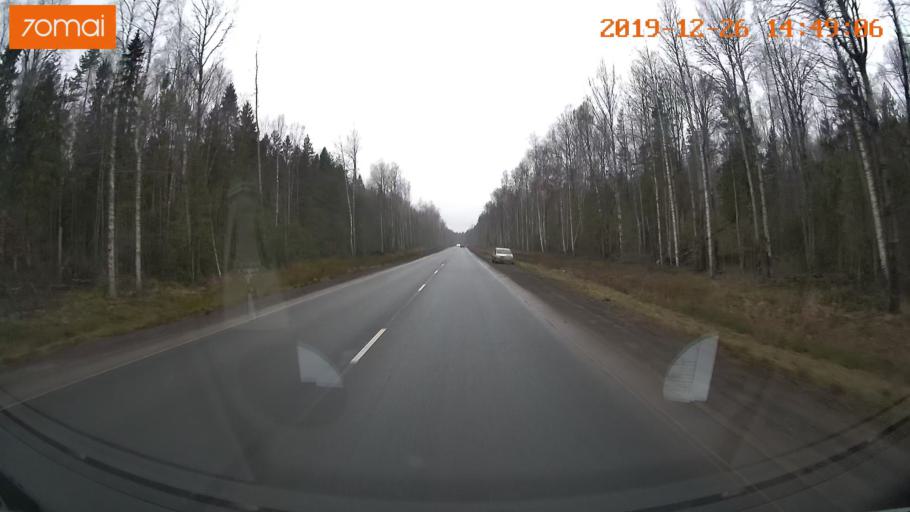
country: RU
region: Jaroslavl
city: Poshekhon'ye
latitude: 58.3408
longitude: 38.9555
